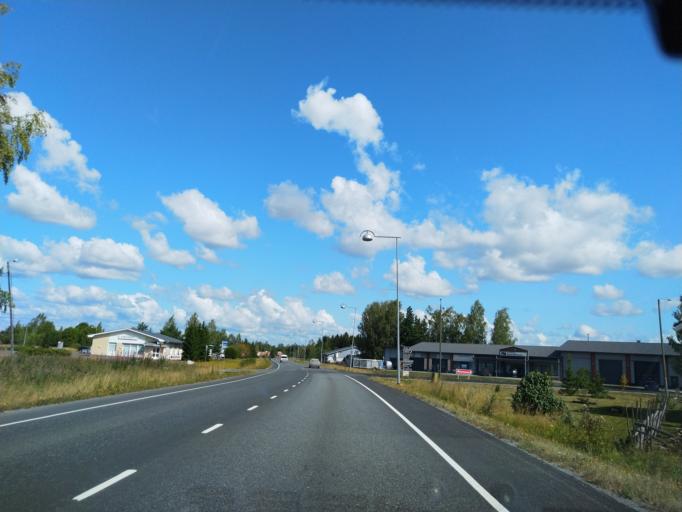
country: FI
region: Satakunta
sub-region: Pori
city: Huittinen
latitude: 61.1683
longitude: 22.7078
